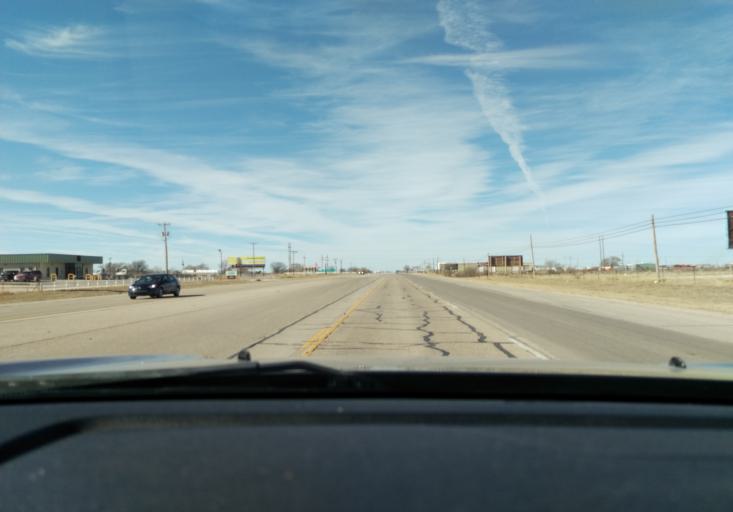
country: US
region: New Mexico
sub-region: Lea County
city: Hobbs
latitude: 32.6967
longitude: -103.1927
